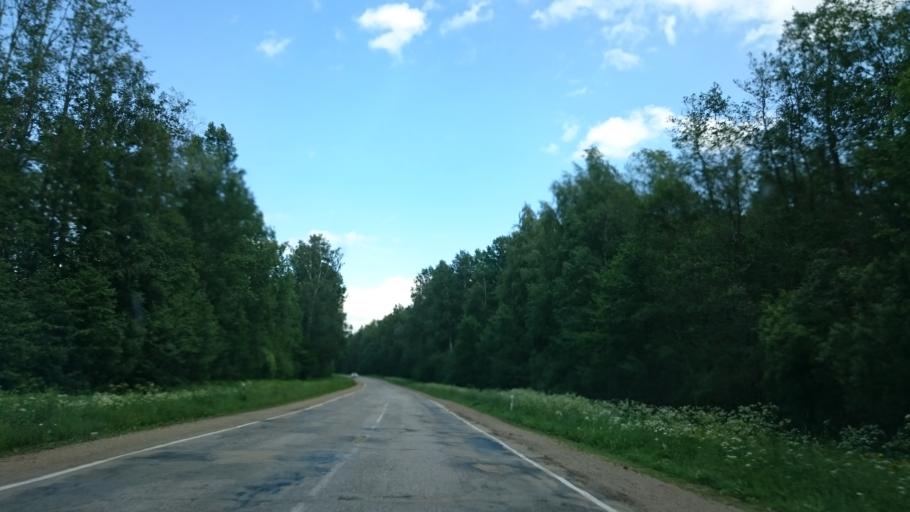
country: LV
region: Ludzas Rajons
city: Ludza
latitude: 56.5349
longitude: 27.6535
